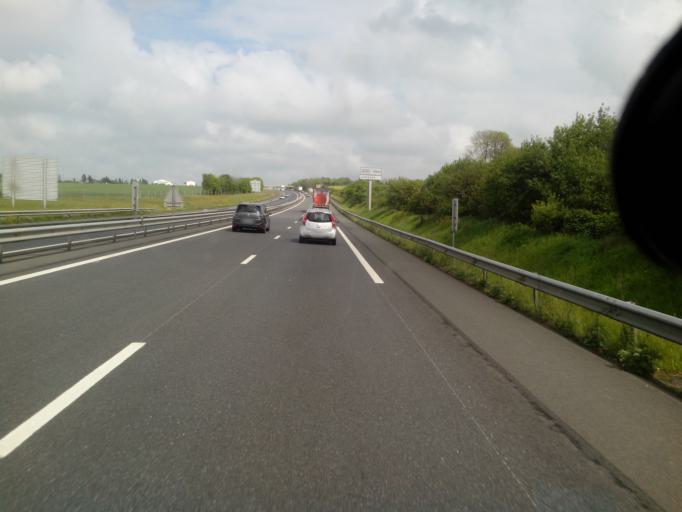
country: FR
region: Lower Normandy
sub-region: Departement du Calvados
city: Cahagnes
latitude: 49.0504
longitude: -0.7370
